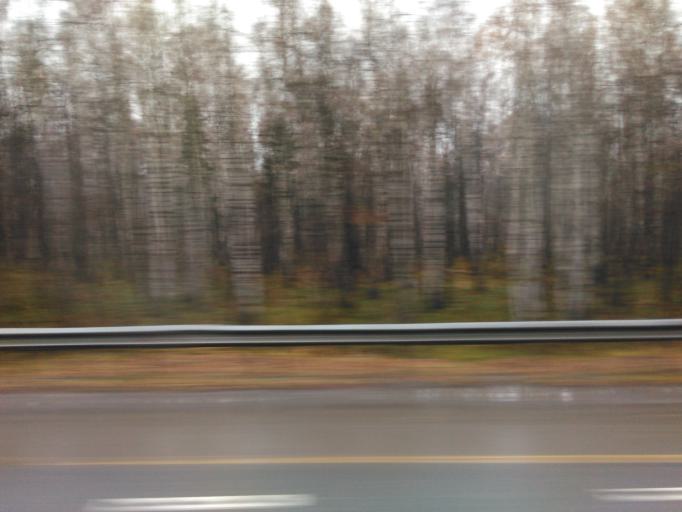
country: RU
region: Tatarstan
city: Osinovo
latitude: 55.8401
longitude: 48.8511
